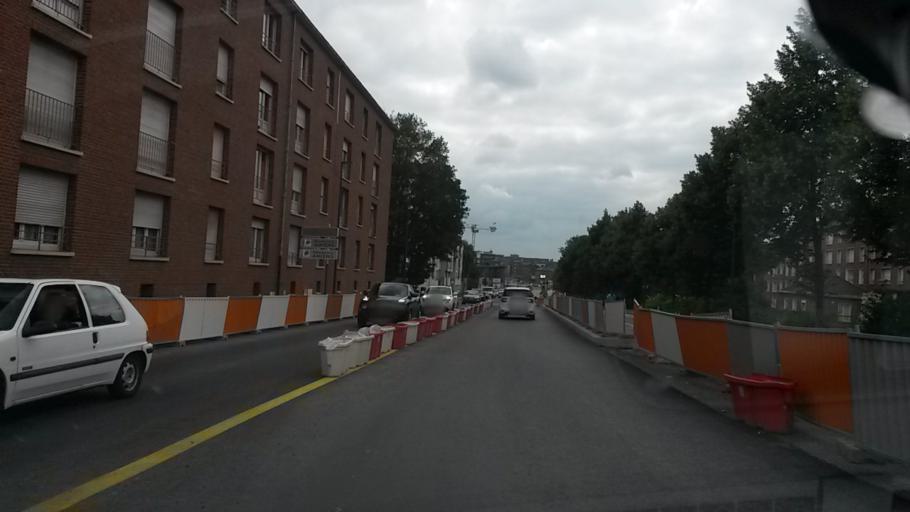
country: FR
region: Picardie
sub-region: Departement de la Somme
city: Amiens
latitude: 49.9014
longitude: 2.2995
